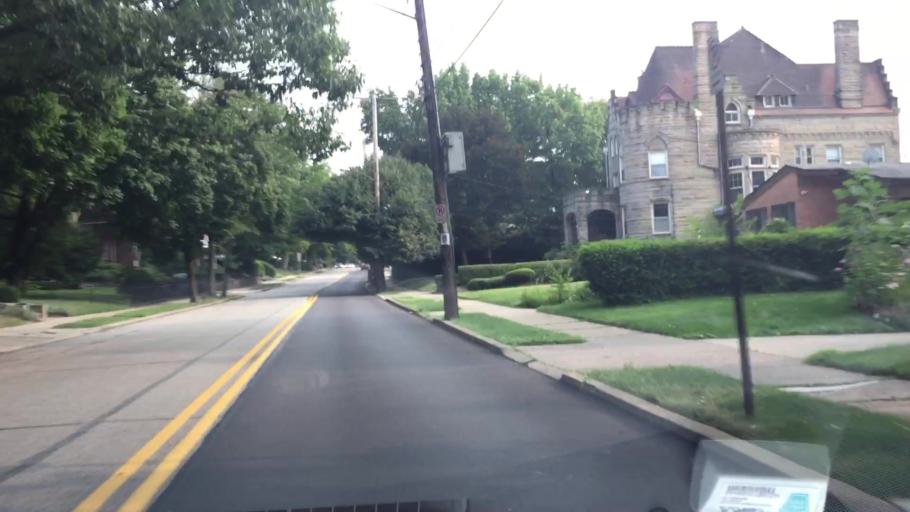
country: US
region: Pennsylvania
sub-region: Allegheny County
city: Bloomfield
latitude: 40.4496
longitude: -79.9428
